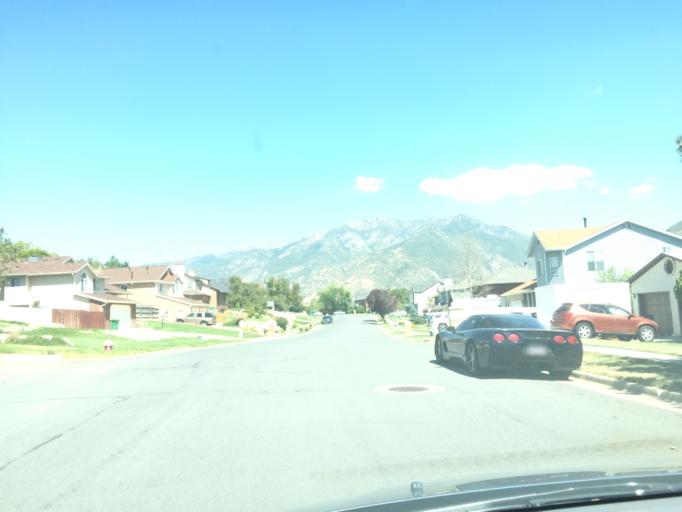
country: US
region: Utah
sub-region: Davis County
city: South Weber
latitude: 41.1105
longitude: -111.9186
